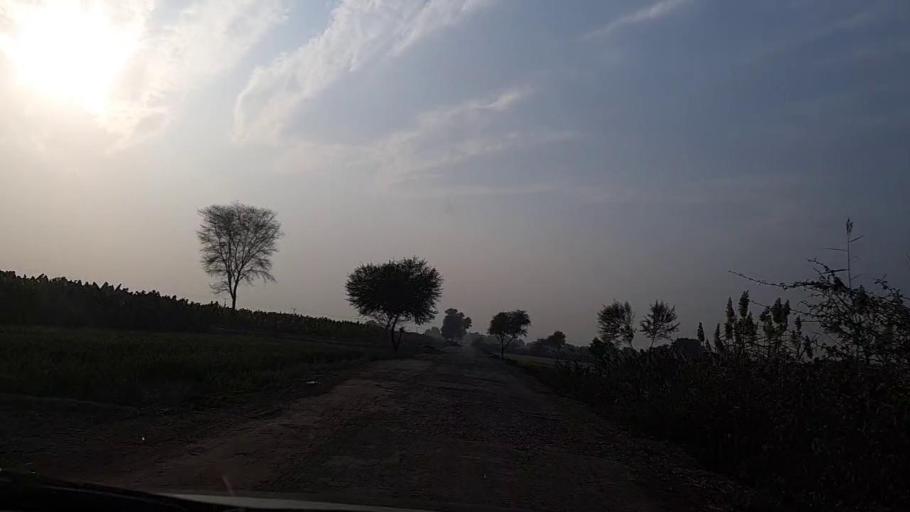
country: PK
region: Sindh
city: Nawabshah
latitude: 26.2833
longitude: 68.3271
